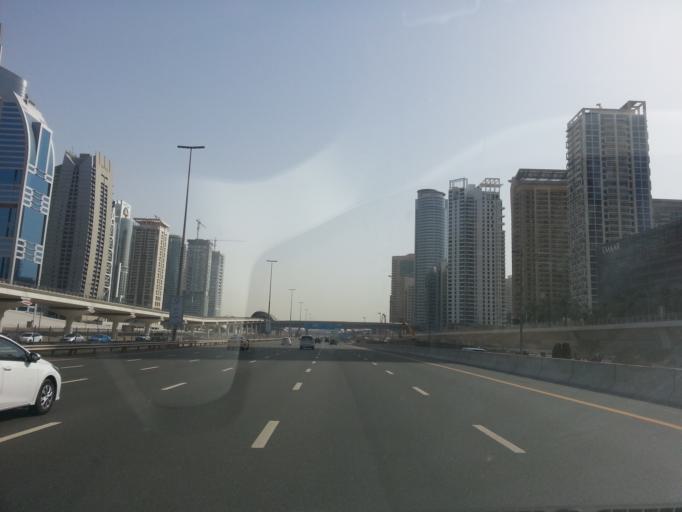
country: AE
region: Dubai
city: Dubai
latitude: 25.0758
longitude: 55.1422
